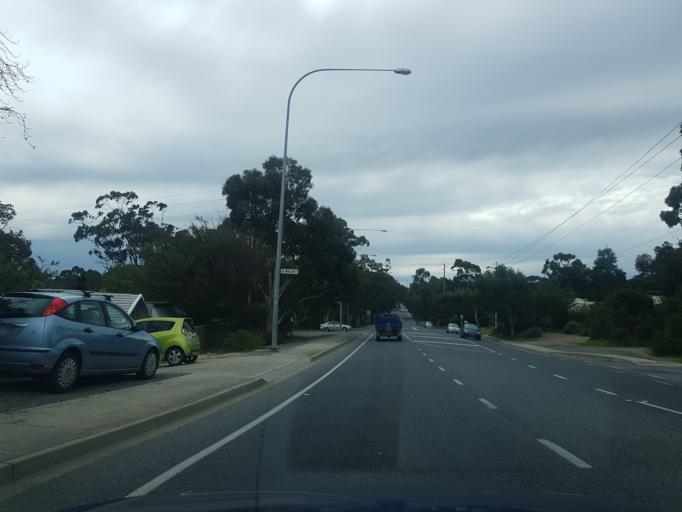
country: AU
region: South Australia
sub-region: Tea Tree Gully
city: Hope Valley
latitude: -34.8326
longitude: 138.7196
